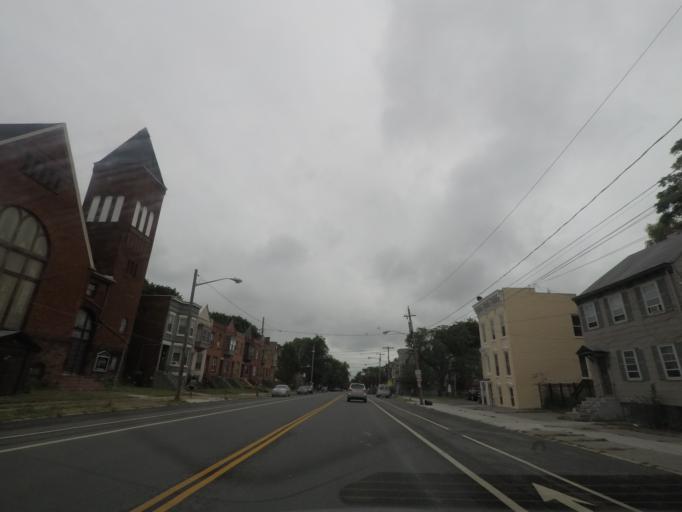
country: US
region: New York
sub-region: Albany County
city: Albany
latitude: 42.6645
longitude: -73.7678
